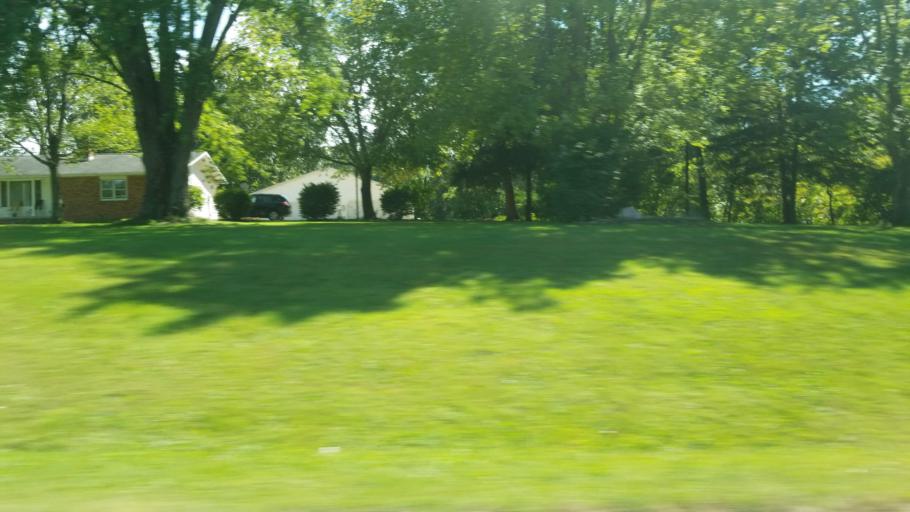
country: US
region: Illinois
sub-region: Williamson County
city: Johnston City
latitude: 37.7894
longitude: -88.8903
